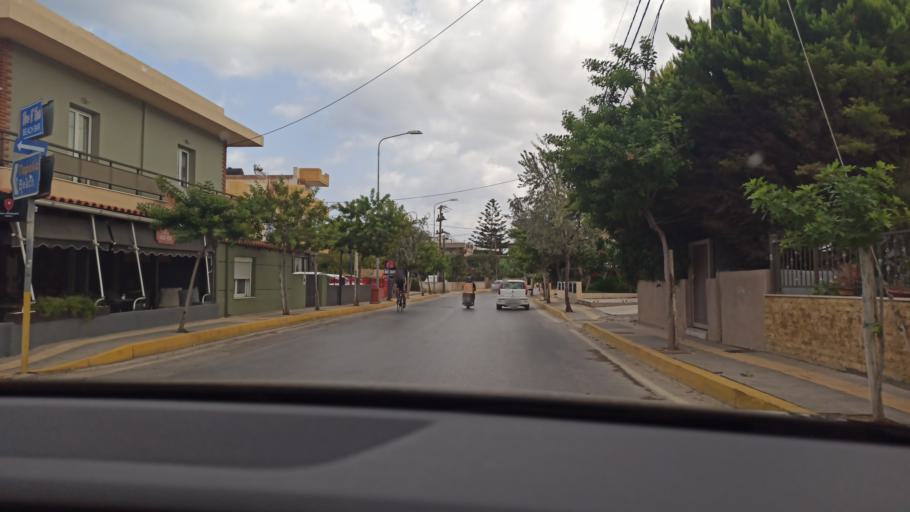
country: GR
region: Crete
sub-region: Nomos Irakleiou
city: Gazi
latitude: 35.3354
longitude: 25.0878
